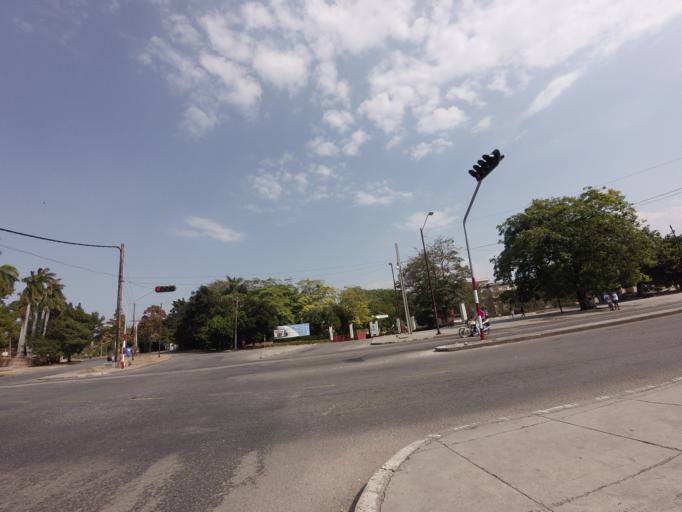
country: CU
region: La Habana
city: Cerro
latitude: 23.0791
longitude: -82.4454
